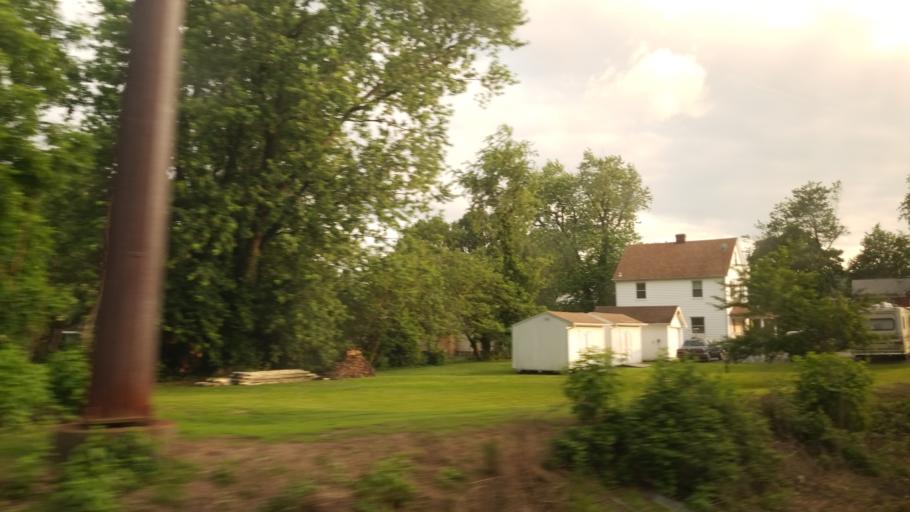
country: US
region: Virginia
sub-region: City of Manassas
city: Manassas
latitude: 38.7512
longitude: -77.4654
